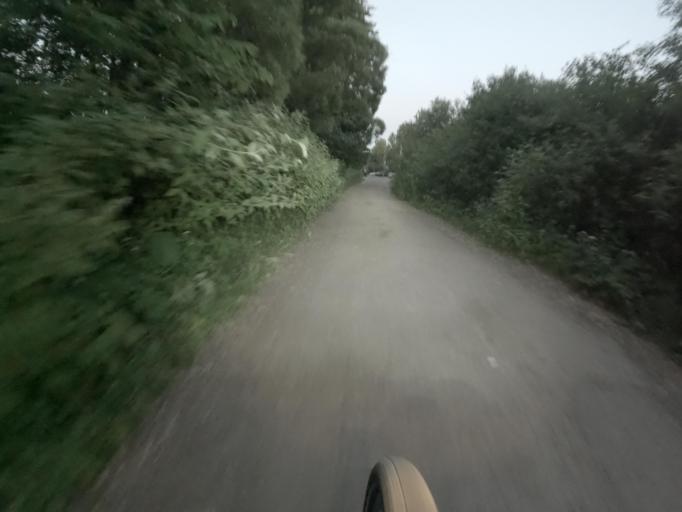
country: RU
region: St.-Petersburg
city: Sapernyy
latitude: 59.7797
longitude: 30.6922
